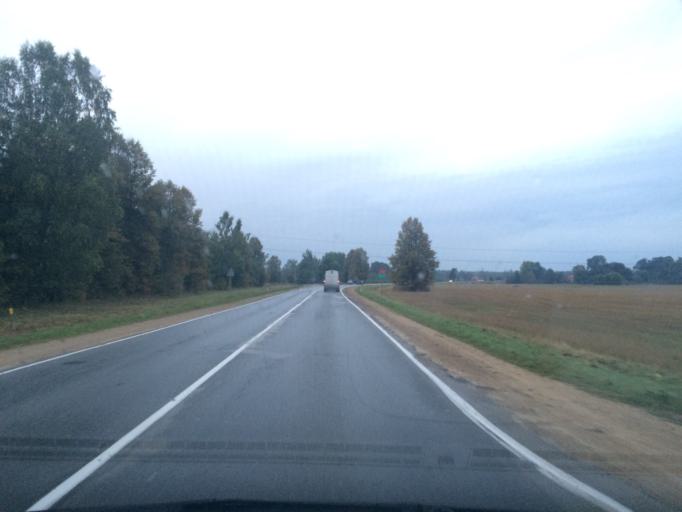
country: LV
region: Plavinu
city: Plavinas
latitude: 56.6015
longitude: 25.7821
